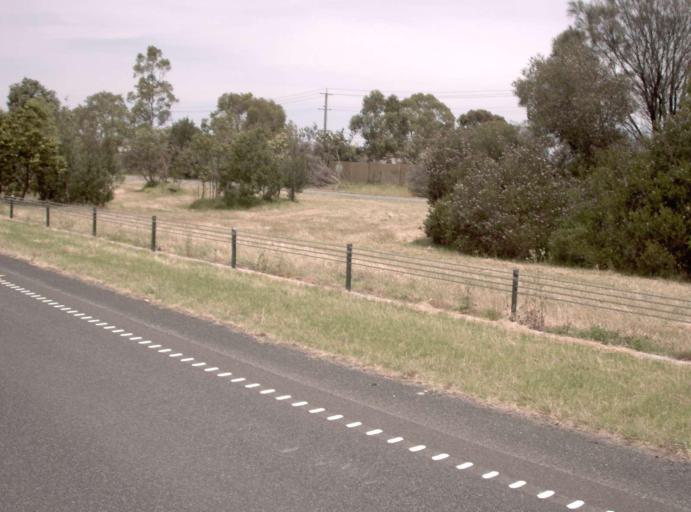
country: AU
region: Victoria
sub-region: Kingston
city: Patterson Lakes
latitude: -38.0785
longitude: 145.1497
